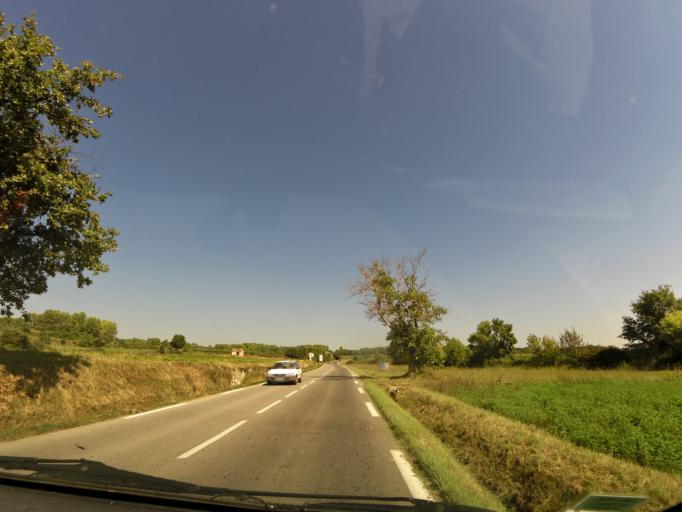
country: FR
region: Languedoc-Roussillon
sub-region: Departement du Gard
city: Villevieille
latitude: 43.8154
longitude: 4.0956
